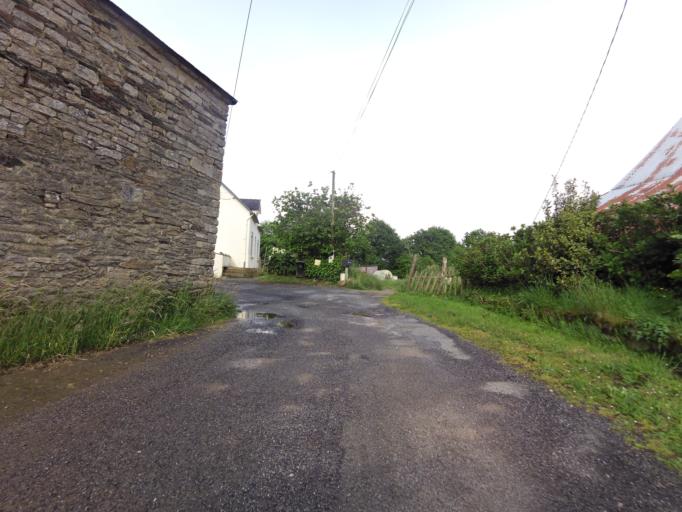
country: FR
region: Brittany
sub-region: Departement du Morbihan
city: Pluherlin
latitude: 47.7115
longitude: -2.3561
